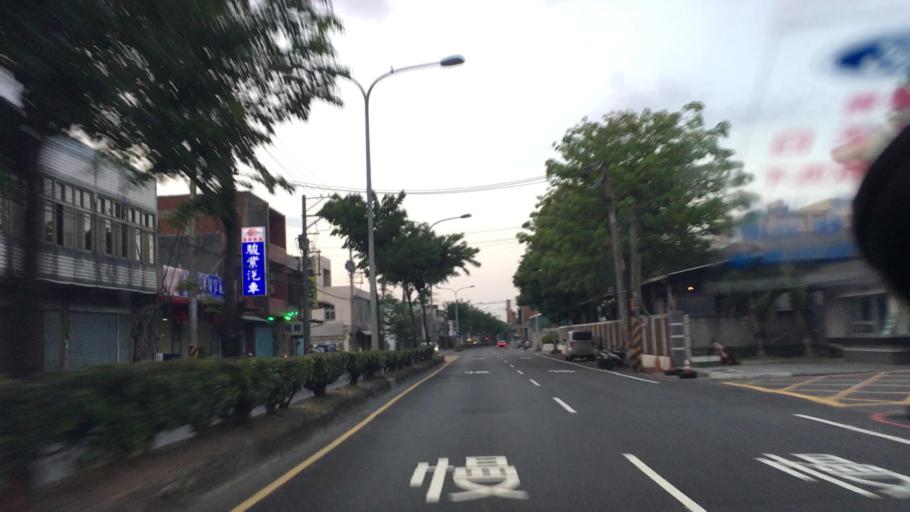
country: TW
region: Taiwan
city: Taoyuan City
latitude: 25.0586
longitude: 121.2677
